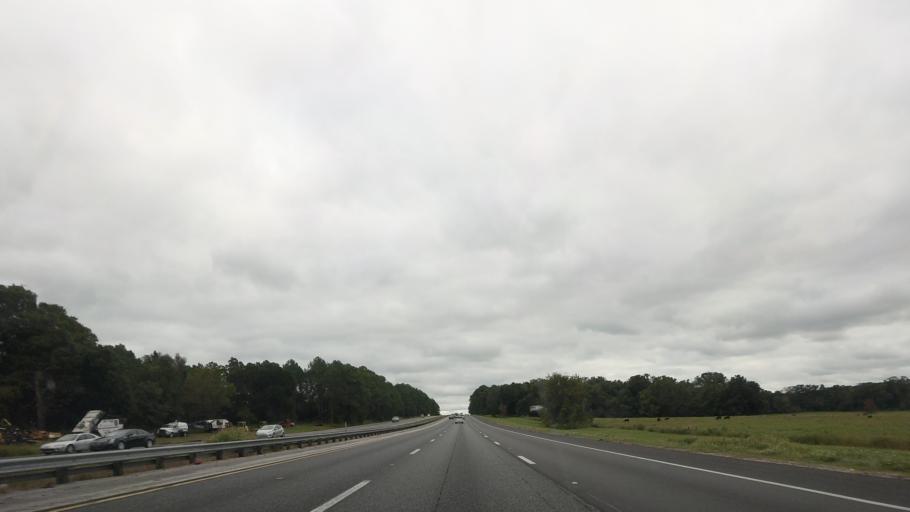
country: US
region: Florida
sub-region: Alachua County
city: High Springs
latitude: 29.8528
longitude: -82.5360
